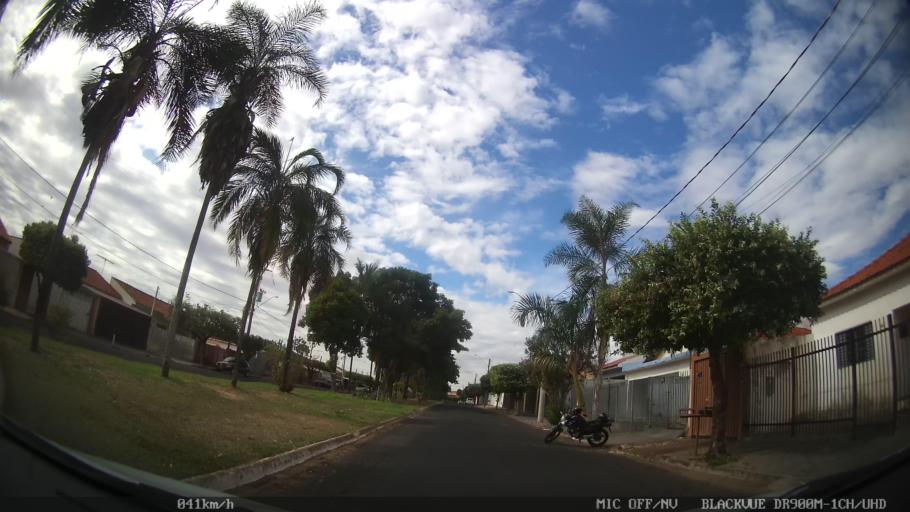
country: BR
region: Sao Paulo
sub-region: Sao Jose Do Rio Preto
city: Sao Jose do Rio Preto
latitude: -20.8086
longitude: -49.4937
